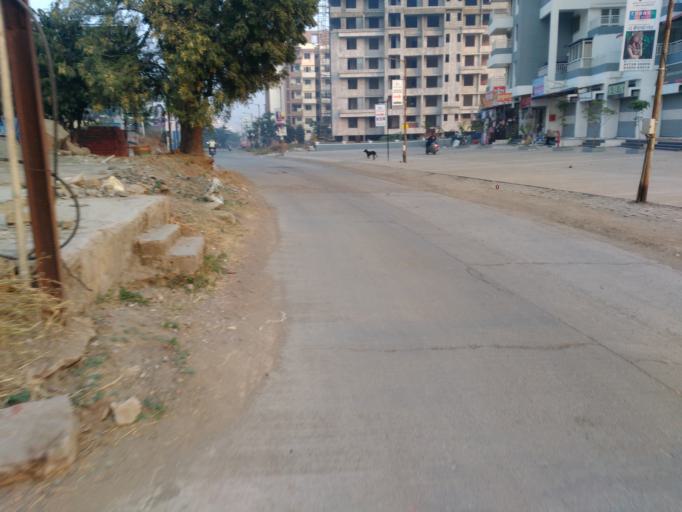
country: IN
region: Maharashtra
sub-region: Pune Division
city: Pune
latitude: 18.4386
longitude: 73.8879
